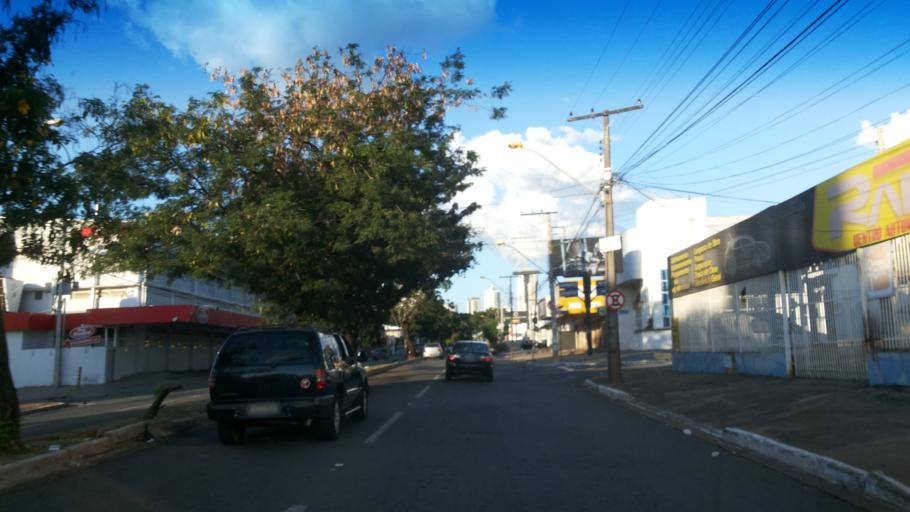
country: BR
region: Goias
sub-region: Goiania
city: Goiania
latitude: -16.7090
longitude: -49.2886
